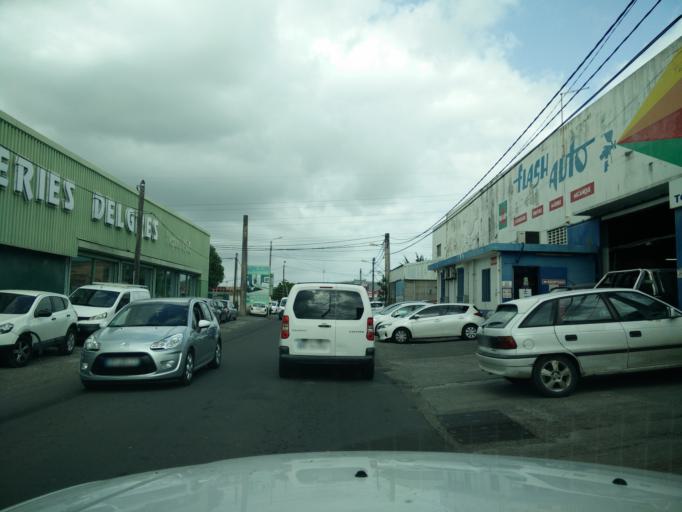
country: GP
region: Guadeloupe
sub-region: Guadeloupe
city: Pointe-a-Pitre
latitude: 16.2371
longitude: -61.5567
